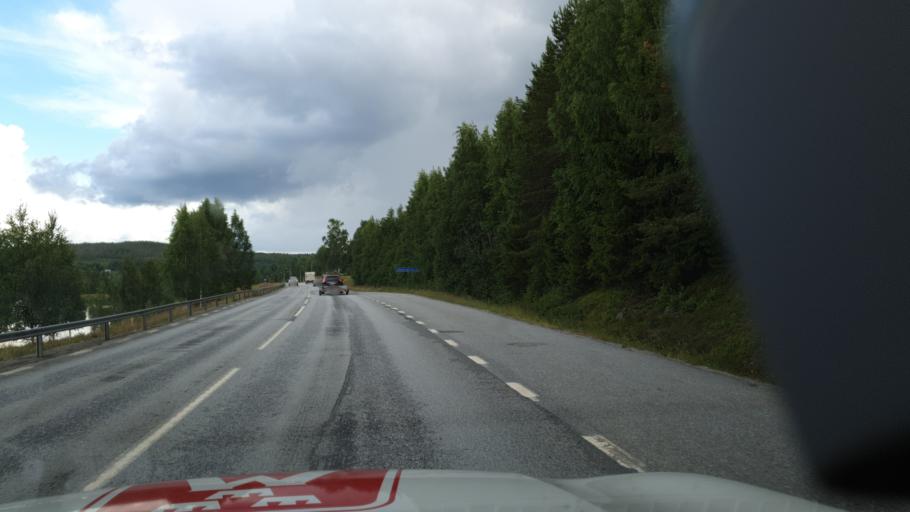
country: SE
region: Vaesterbotten
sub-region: Vannas Kommun
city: Vannasby
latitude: 64.0026
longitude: 20.0348
